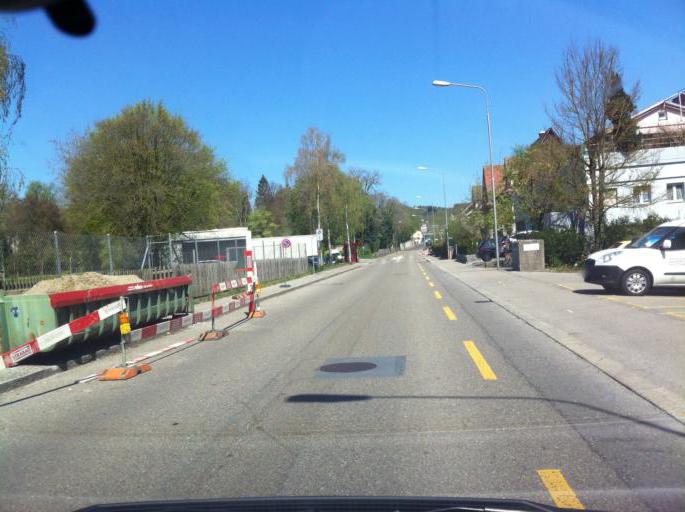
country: CH
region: Schaffhausen
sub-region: Bezirk Schaffhausen
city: Schaffhausen
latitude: 47.7031
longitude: 8.6273
